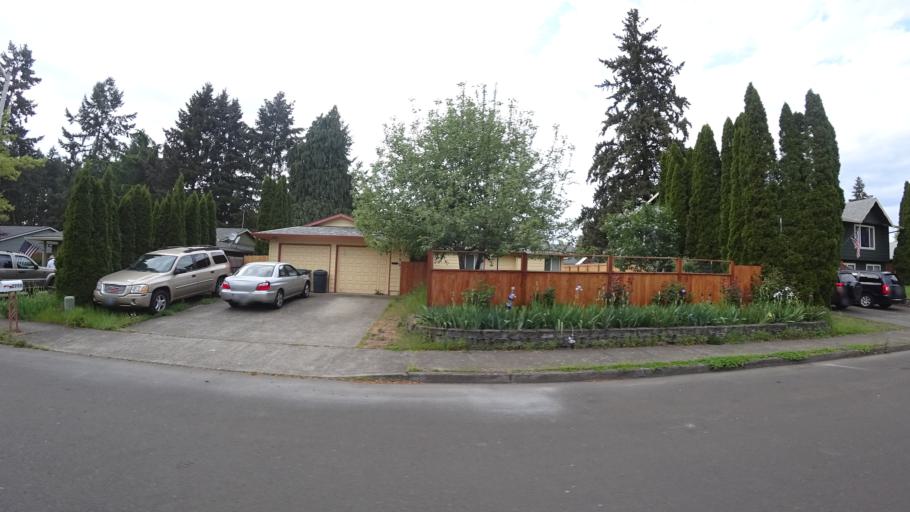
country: US
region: Oregon
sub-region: Washington County
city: Hillsboro
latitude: 45.4985
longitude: -122.9536
